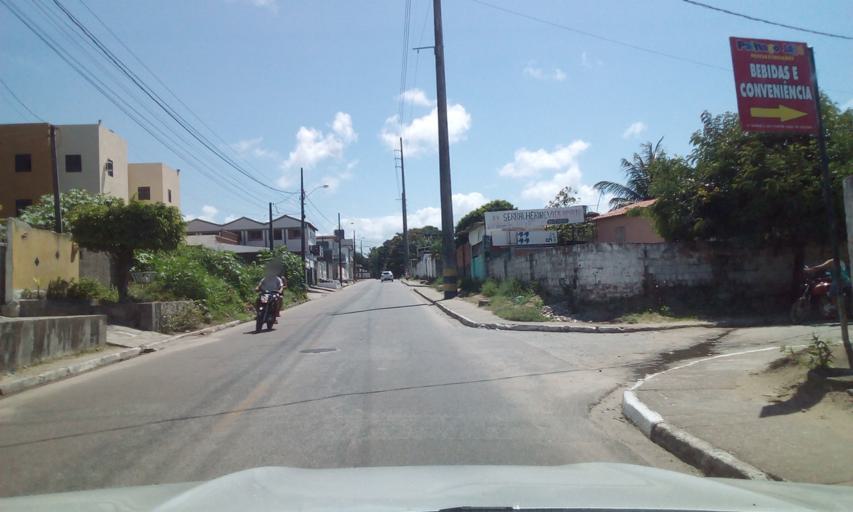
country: BR
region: Paraiba
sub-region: Conde
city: Conde
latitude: -7.2097
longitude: -34.8404
